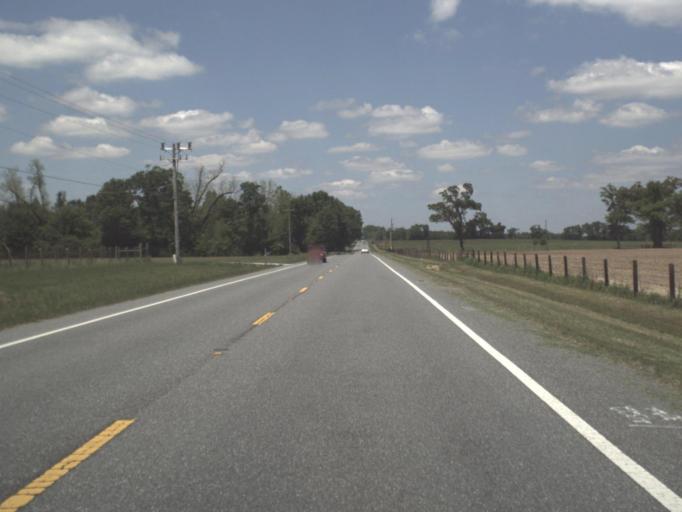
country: US
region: Florida
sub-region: Santa Rosa County
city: Point Baker
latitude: 30.8223
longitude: -87.0465
